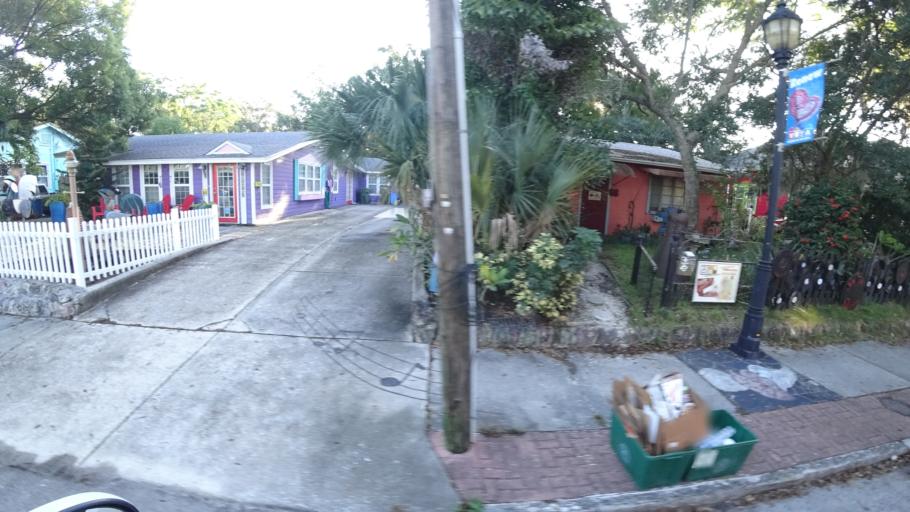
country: US
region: Florida
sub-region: Manatee County
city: Bradenton
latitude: 27.4895
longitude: -82.5732
